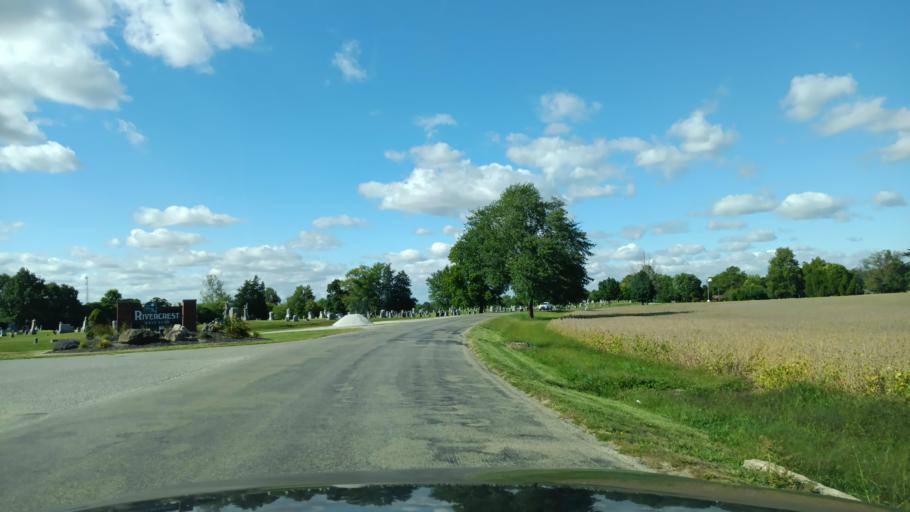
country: US
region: Indiana
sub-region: Fountain County
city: Covington
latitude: 40.1281
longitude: -87.3854
